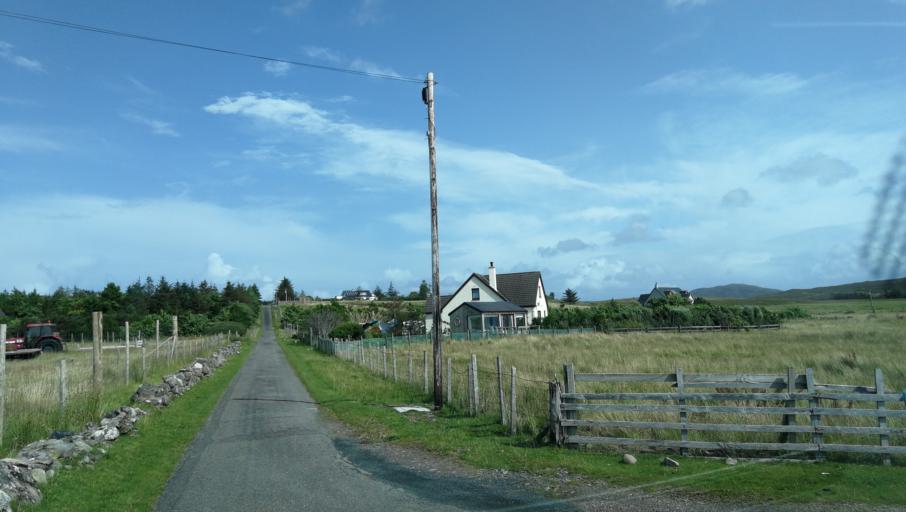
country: GB
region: Scotland
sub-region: Highland
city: Portree
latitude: 57.7430
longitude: -5.7771
